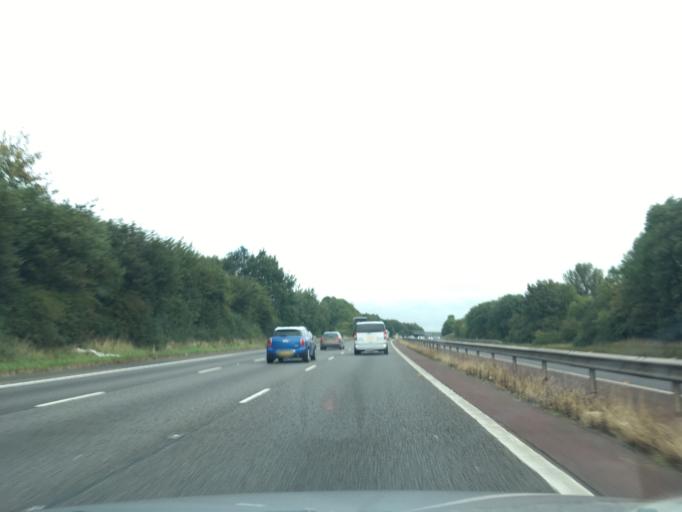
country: GB
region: England
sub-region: Oxfordshire
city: Adderbury
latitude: 52.0334
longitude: -1.3020
